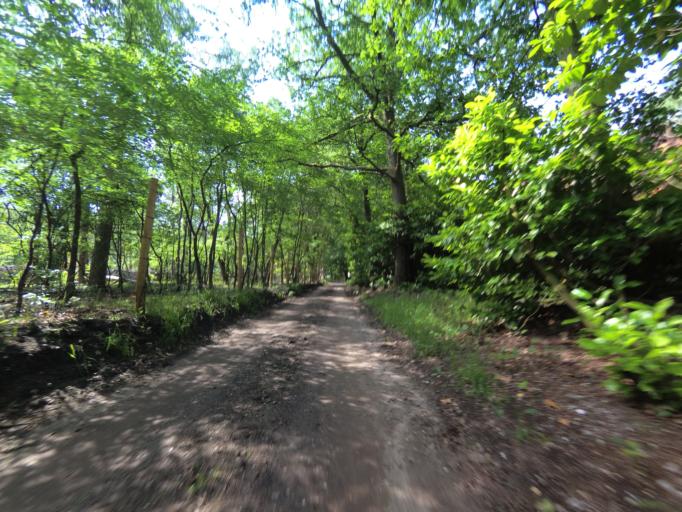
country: NL
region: Gelderland
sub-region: Gemeente Apeldoorn
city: Beekbergen
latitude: 52.1070
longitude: 5.8839
